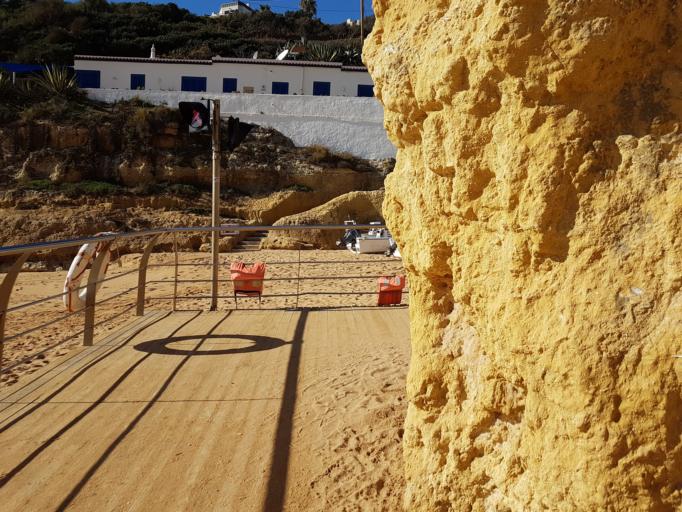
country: PT
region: Faro
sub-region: Lagoa
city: Carvoeiro
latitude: 37.0874
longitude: -8.4263
